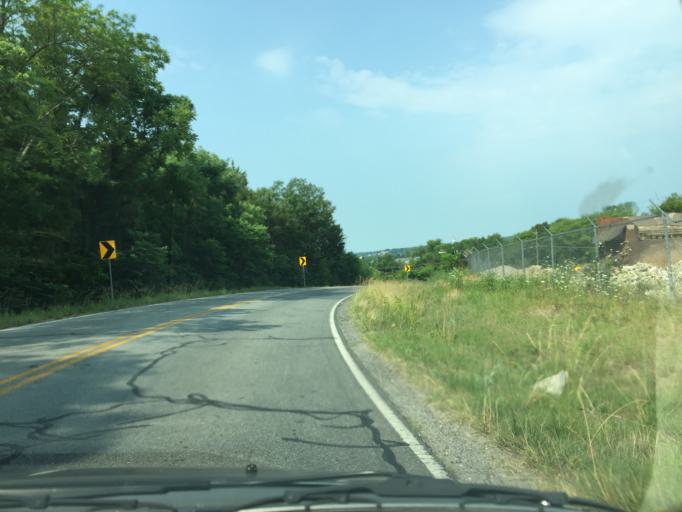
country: US
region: Georgia
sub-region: Catoosa County
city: Ringgold
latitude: 34.9189
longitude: -85.1047
